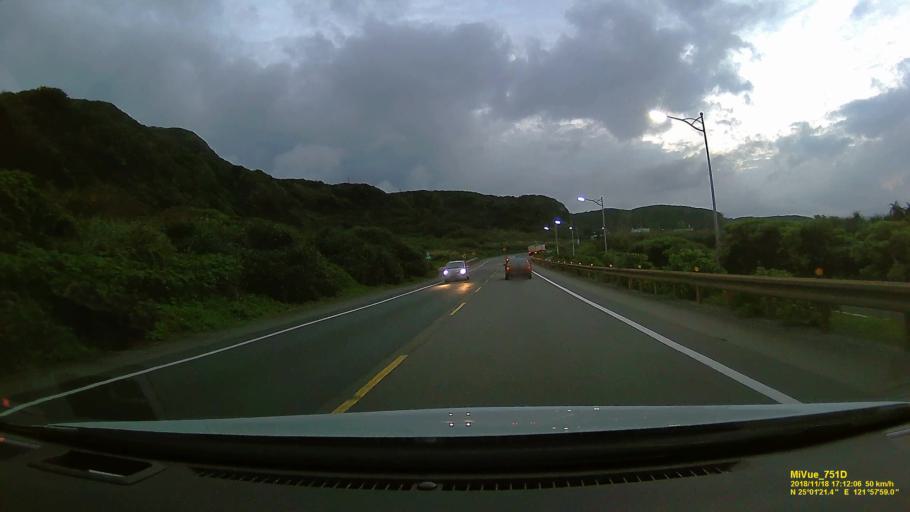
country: TW
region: Taiwan
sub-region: Keelung
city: Keelung
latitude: 25.0225
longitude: 121.9663
